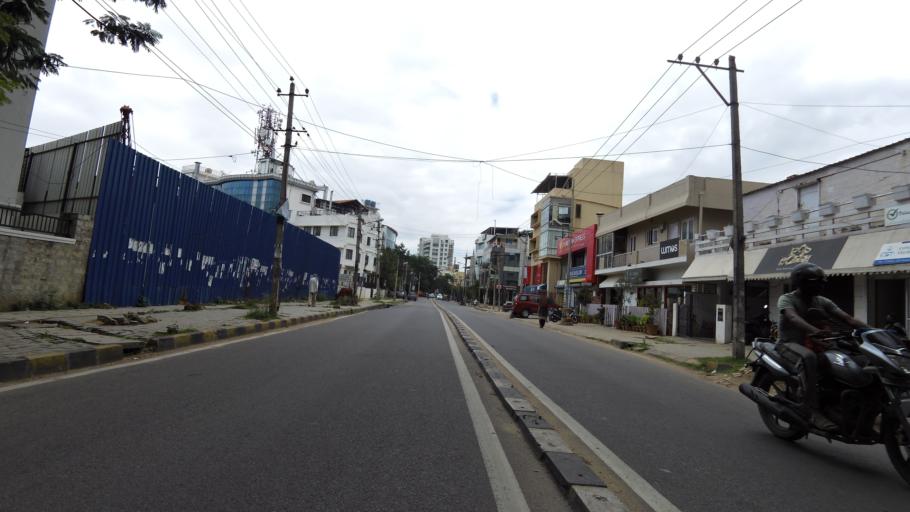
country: IN
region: Karnataka
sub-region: Bangalore Urban
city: Bangalore
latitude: 12.9682
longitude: 77.6363
